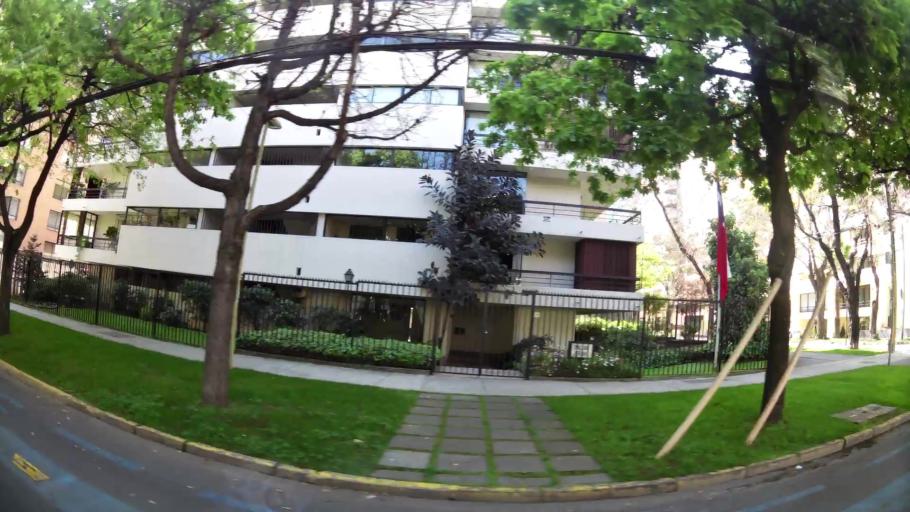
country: CL
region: Santiago Metropolitan
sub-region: Provincia de Santiago
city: Villa Presidente Frei, Nunoa, Santiago, Chile
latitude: -33.4180
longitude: -70.5925
